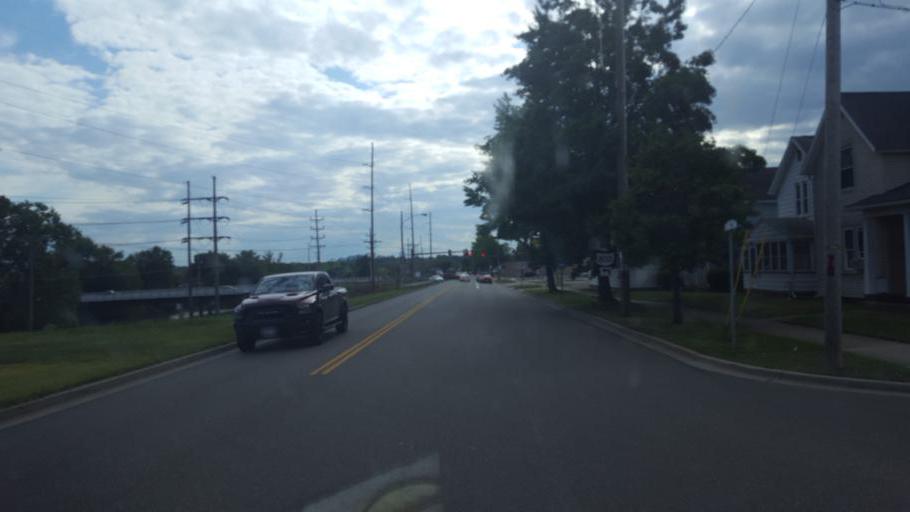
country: US
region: Ohio
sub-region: Tuscarawas County
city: Dover
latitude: 40.5216
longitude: -81.4728
